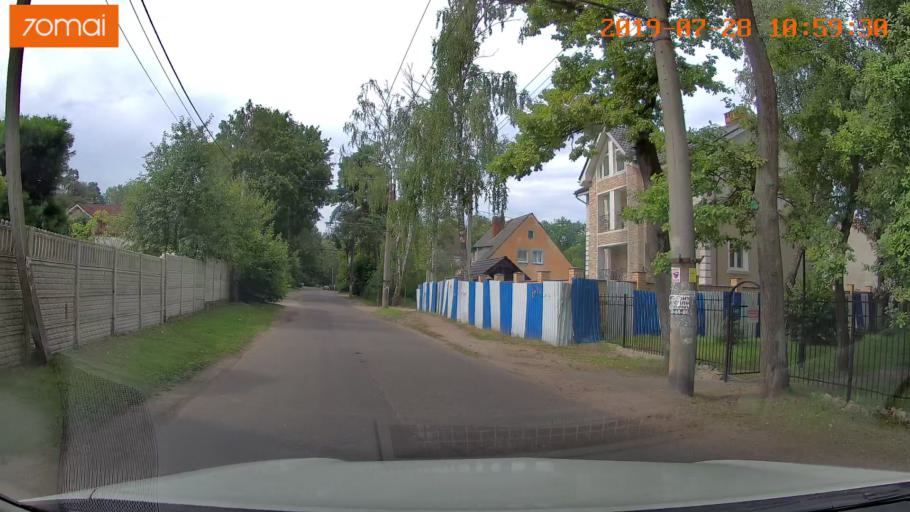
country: RU
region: Kaliningrad
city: Vzmorye
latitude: 54.7283
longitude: 20.3568
